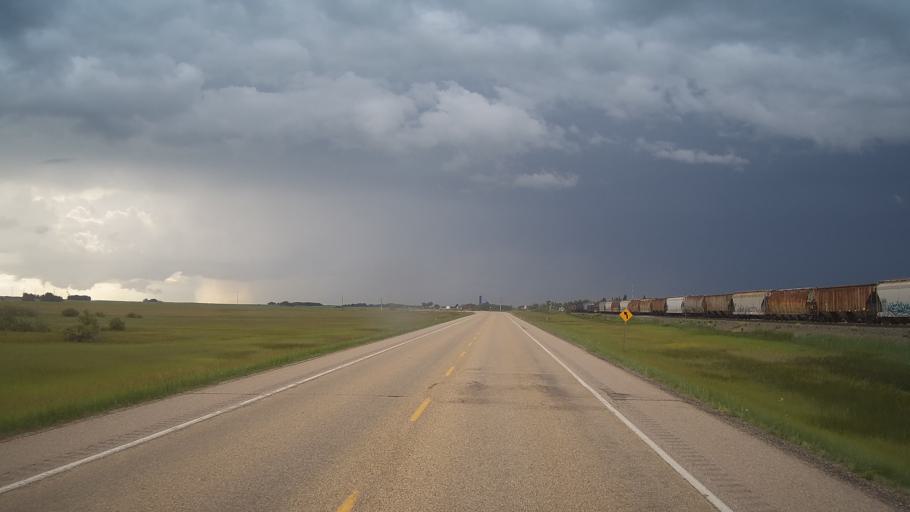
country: CA
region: Alberta
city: Tofield
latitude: 53.2813
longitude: -112.4085
